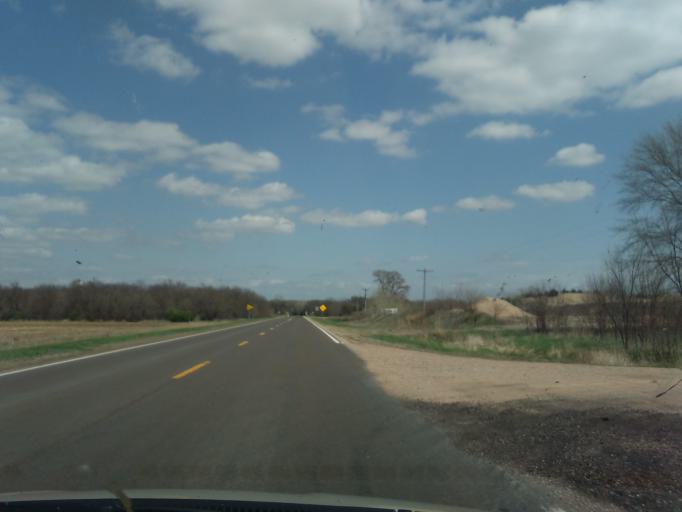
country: US
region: Nebraska
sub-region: Thayer County
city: Hebron
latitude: 40.2489
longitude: -97.5696
